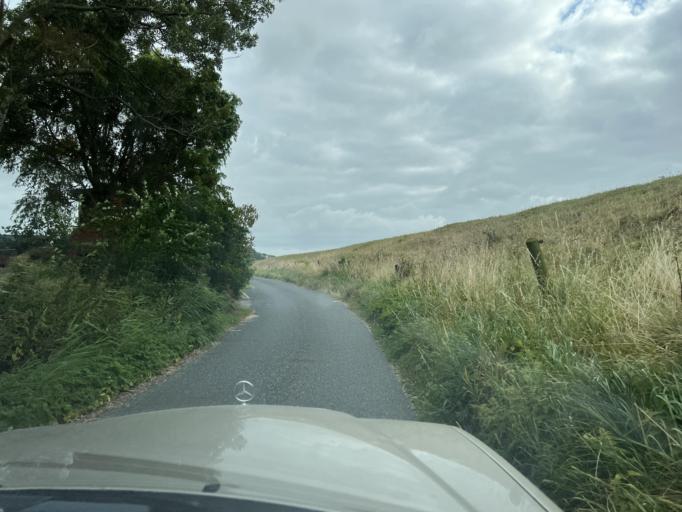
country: DE
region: Schleswig-Holstein
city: Groven
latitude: 54.3122
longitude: 8.9843
